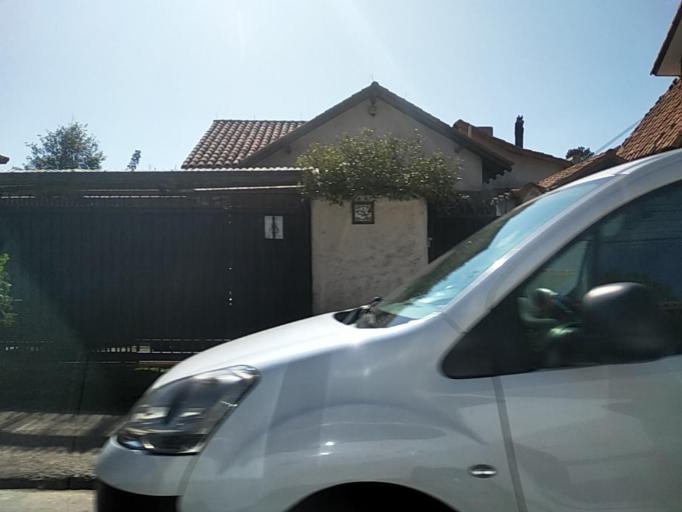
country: CL
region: Valparaiso
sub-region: Provincia de Valparaiso
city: Vina del Mar
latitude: -32.9389
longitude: -71.5396
